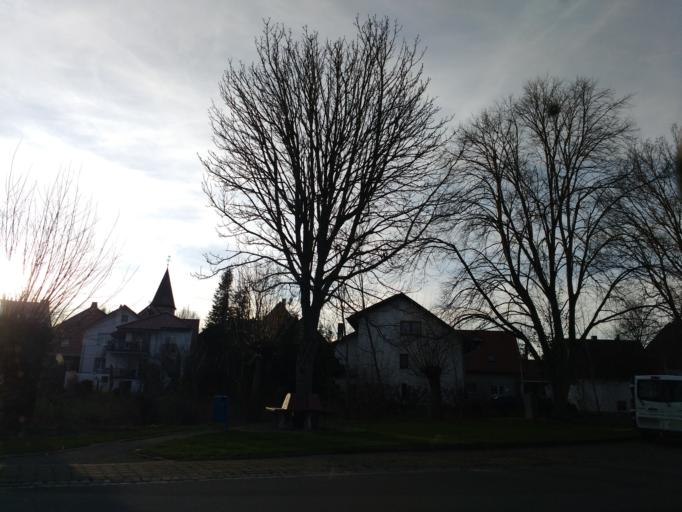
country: DE
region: North Rhine-Westphalia
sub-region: Regierungsbezirk Detmold
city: Salzkotten
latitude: 51.6560
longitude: 8.6024
